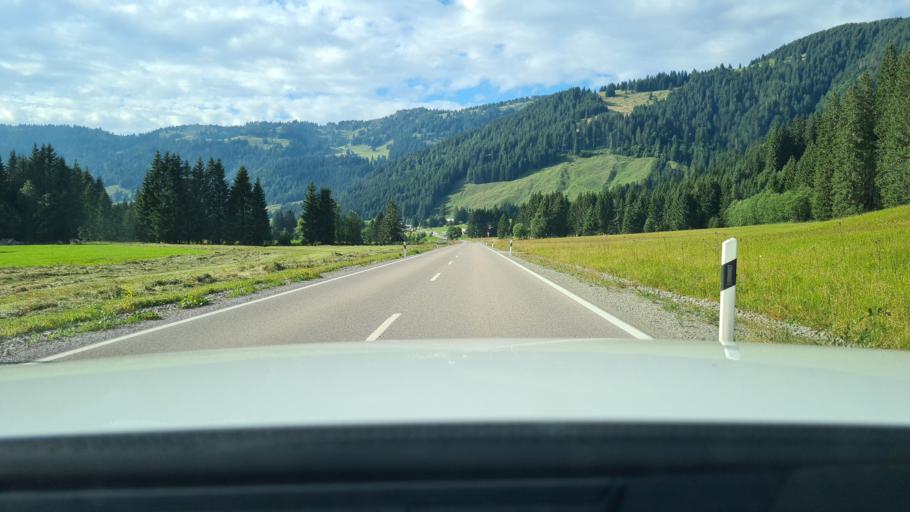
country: DE
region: Bavaria
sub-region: Swabia
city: Balderschwang
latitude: 47.4499
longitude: 10.1337
